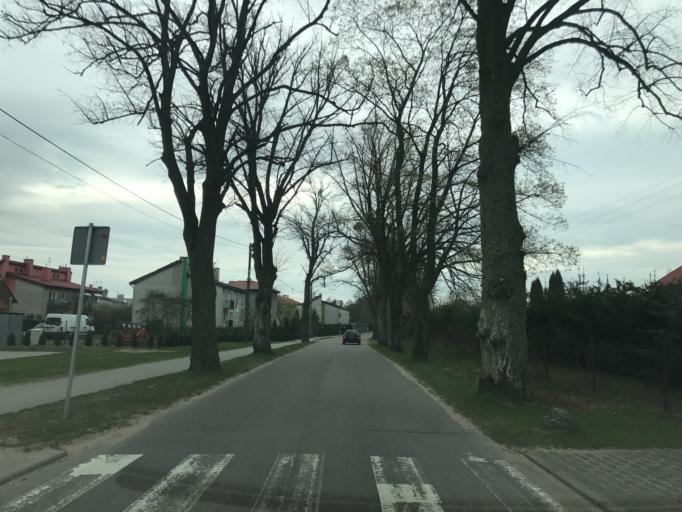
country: PL
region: Warmian-Masurian Voivodeship
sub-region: Powiat olsztynski
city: Olsztynek
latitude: 53.5884
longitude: 20.2798
